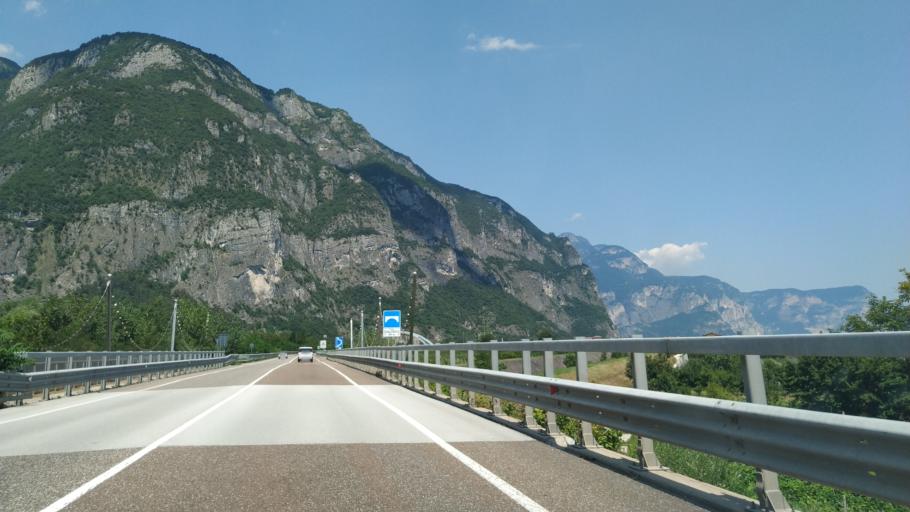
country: IT
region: Trentino-Alto Adige
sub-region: Provincia di Trento
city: Zambana
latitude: 46.1513
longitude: 11.0769
